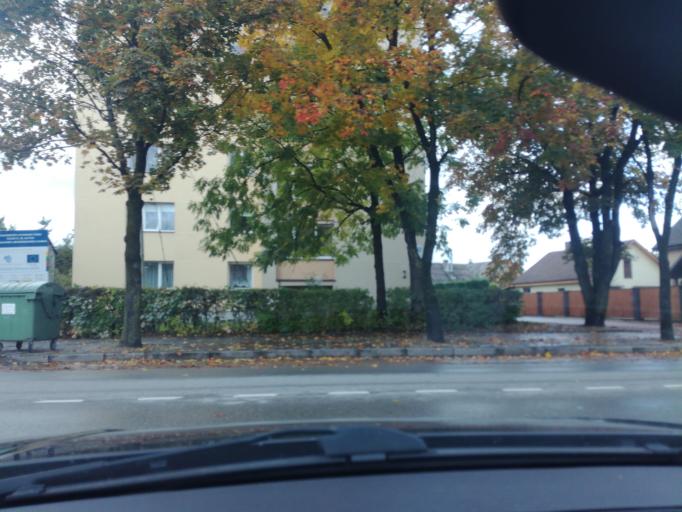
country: LT
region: Alytaus apskritis
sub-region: Alytus
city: Alytus
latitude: 54.3910
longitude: 24.0442
